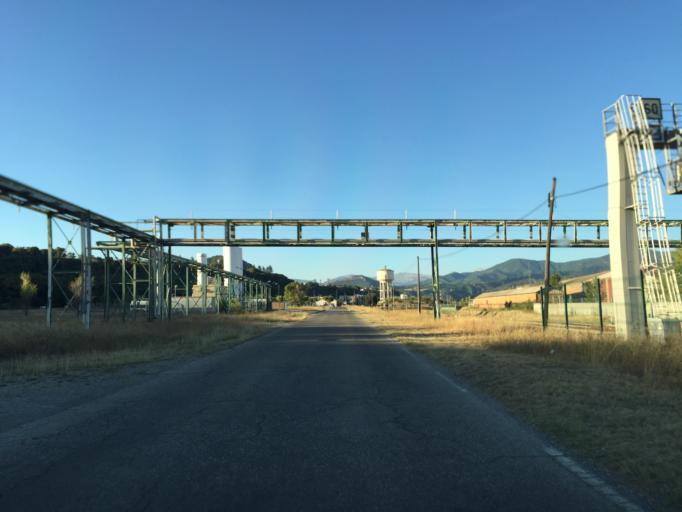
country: FR
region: Provence-Alpes-Cote d'Azur
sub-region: Departement des Alpes-de-Haute-Provence
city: Malijai
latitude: 44.0634
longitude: 5.9979
